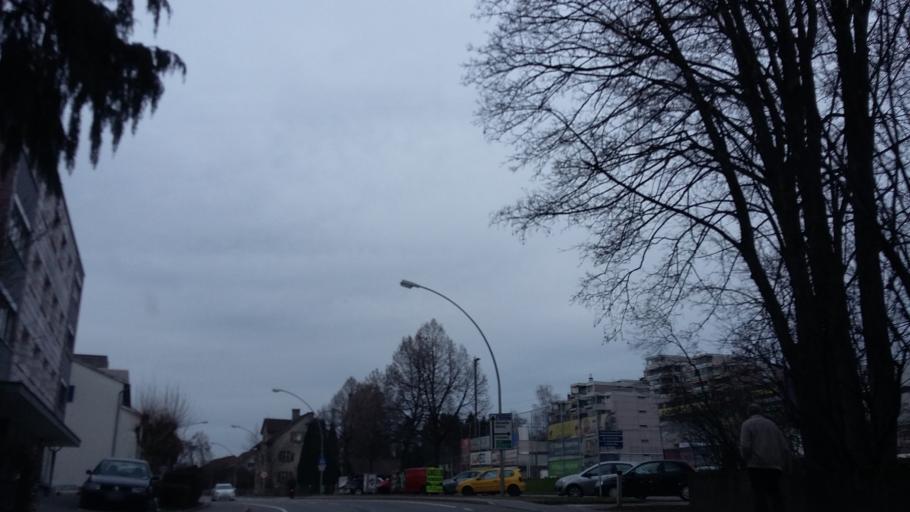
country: AT
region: Vorarlberg
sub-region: Politischer Bezirk Bregenz
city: Lochau
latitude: 47.5315
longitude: 9.7520
